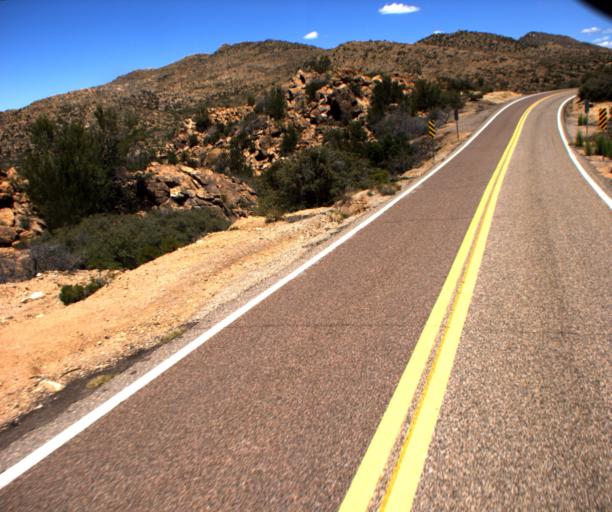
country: US
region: Arizona
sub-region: Yavapai County
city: Bagdad
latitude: 34.4442
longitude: -112.9408
